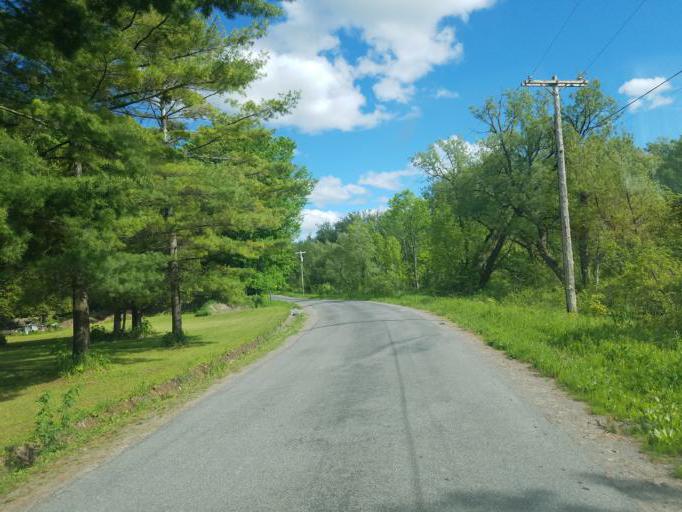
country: US
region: New York
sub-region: Herkimer County
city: Ilion
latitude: 42.9662
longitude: -75.0391
